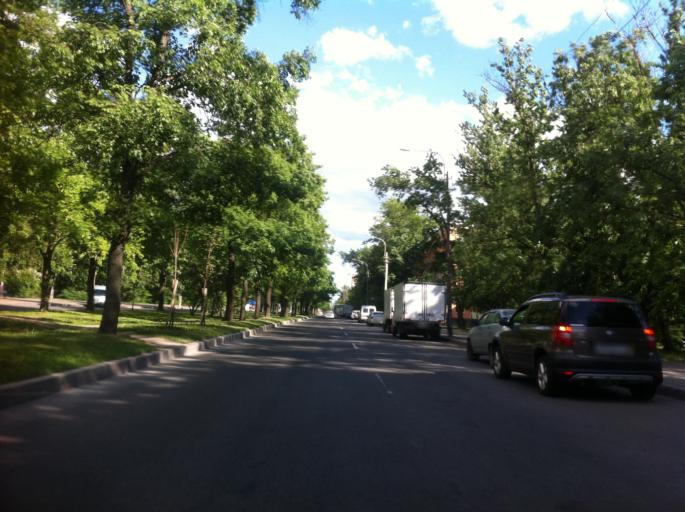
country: RU
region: St.-Petersburg
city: Dachnoye
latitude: 59.8460
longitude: 30.2597
